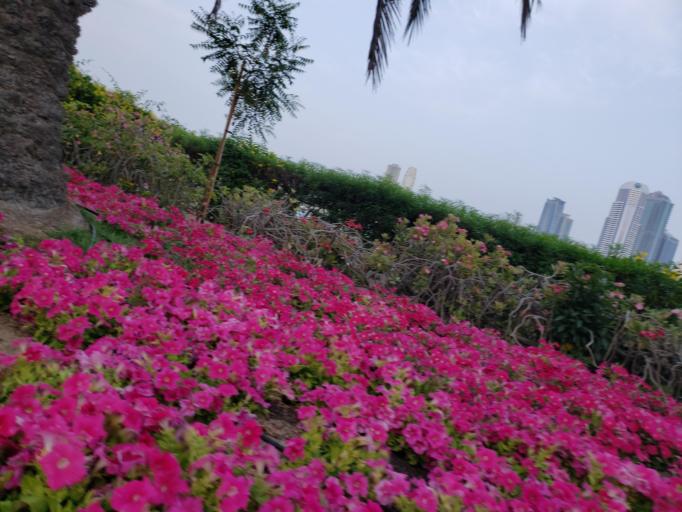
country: AE
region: Ash Shariqah
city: Sharjah
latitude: 25.3173
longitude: 55.3498
